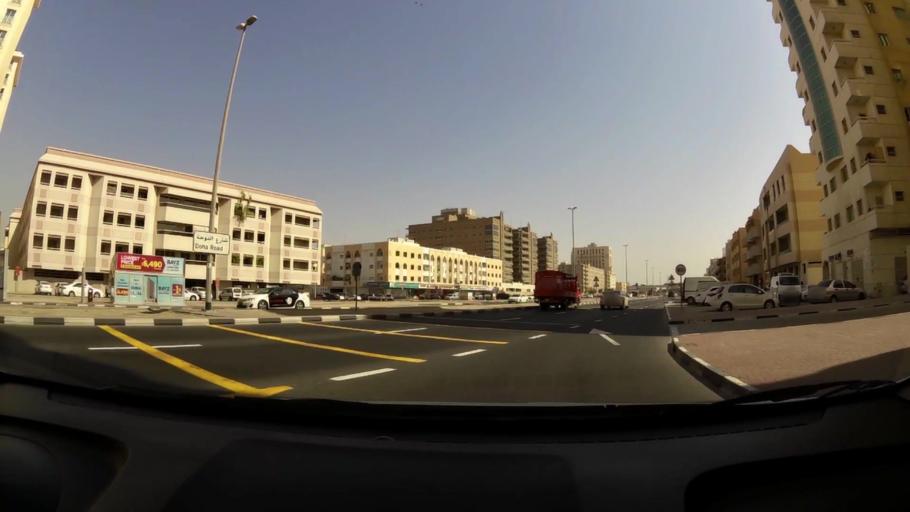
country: AE
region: Ash Shariqah
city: Sharjah
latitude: 25.2763
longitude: 55.3746
